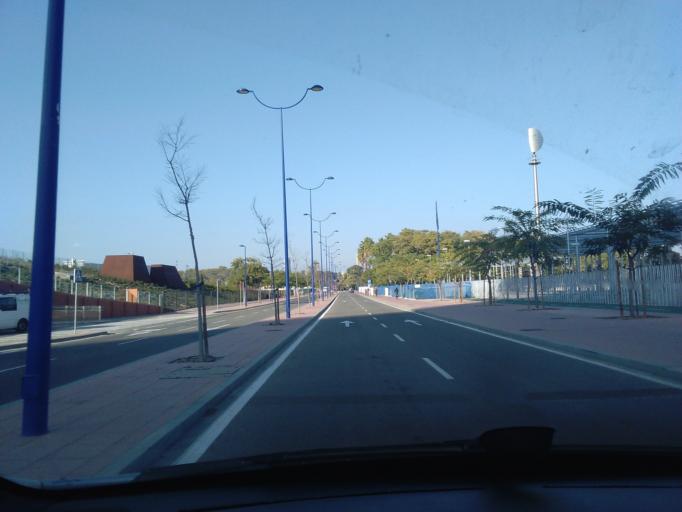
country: ES
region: Andalusia
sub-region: Provincia de Sevilla
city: Camas
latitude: 37.3925
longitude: -6.0090
